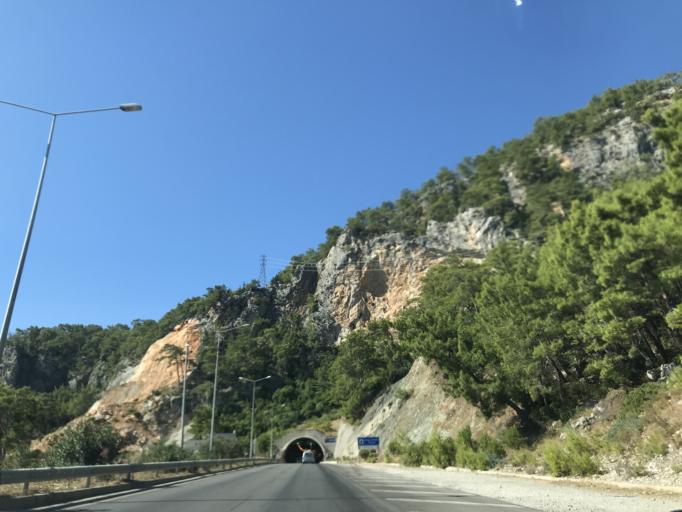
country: TR
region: Antalya
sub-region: Kemer
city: Goeynuek
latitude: 36.7520
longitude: 30.5670
